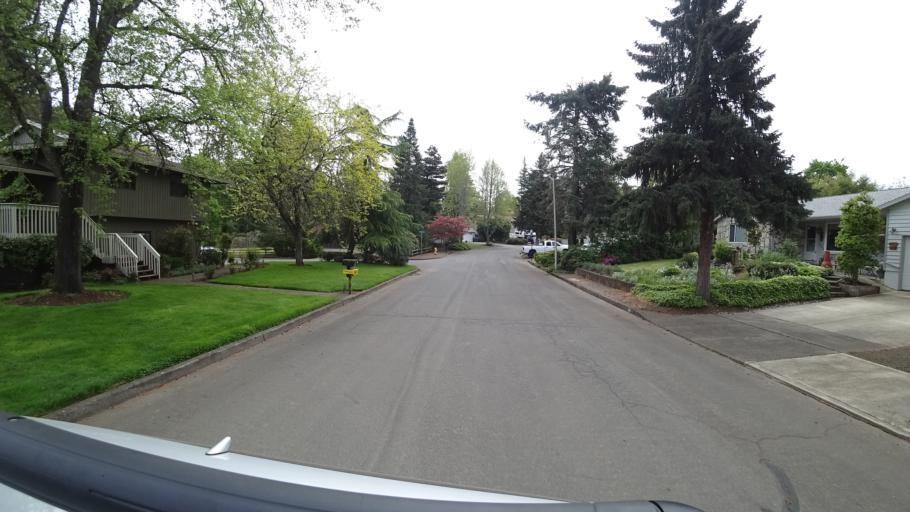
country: US
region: Oregon
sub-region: Washington County
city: Hillsboro
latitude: 45.5319
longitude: -122.9992
